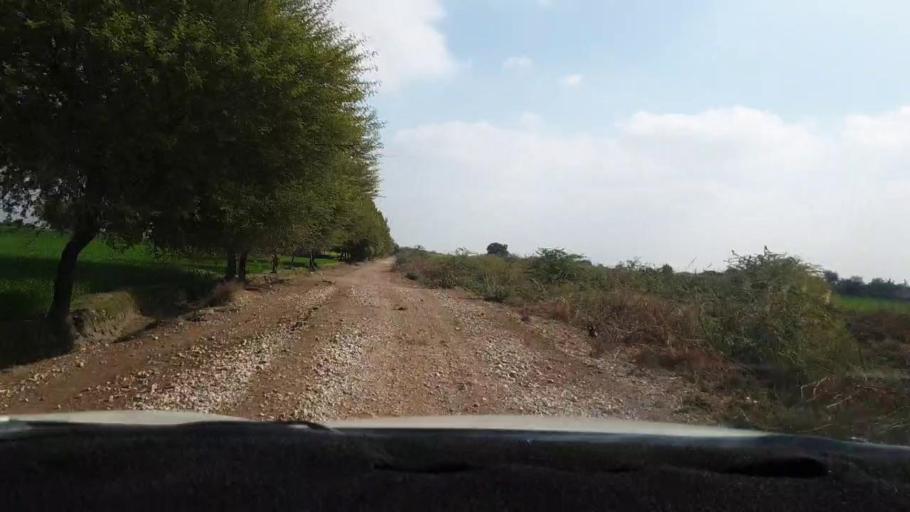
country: PK
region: Sindh
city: Berani
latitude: 25.7777
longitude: 68.9836
